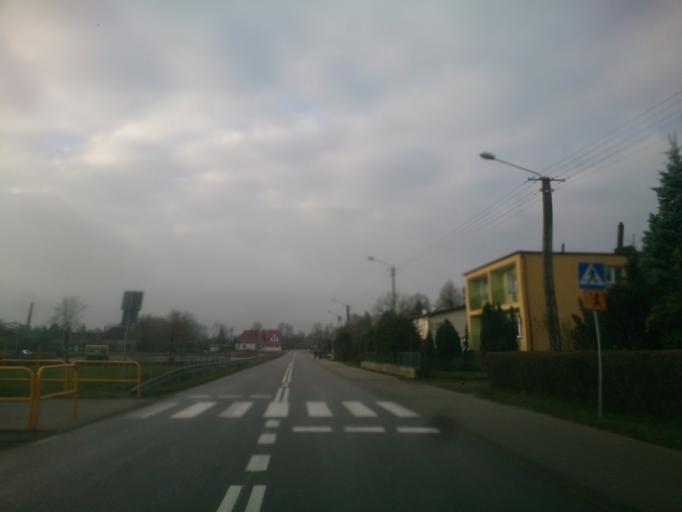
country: PL
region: Pomeranian Voivodeship
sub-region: Powiat czluchowski
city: Koczala
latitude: 54.0229
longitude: 17.1725
